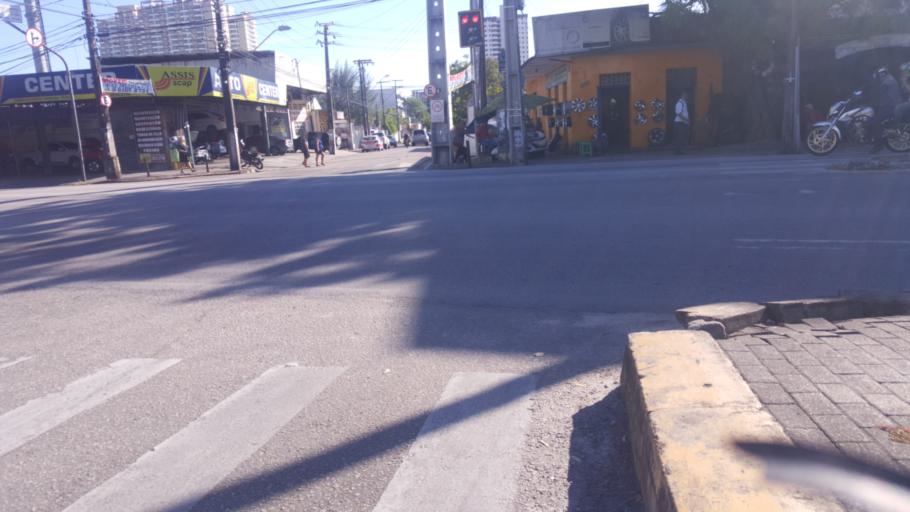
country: BR
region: Ceara
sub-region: Fortaleza
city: Fortaleza
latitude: -3.7452
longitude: -38.5342
